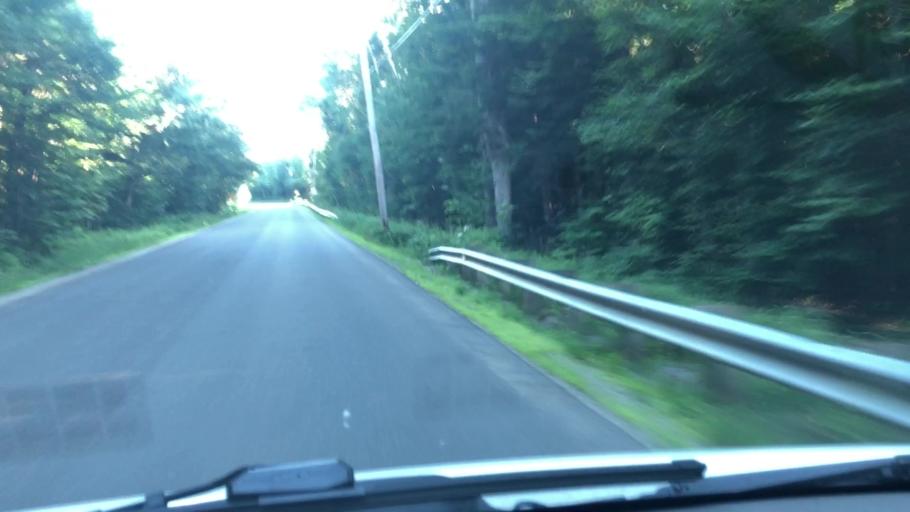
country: US
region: Massachusetts
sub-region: Berkshire County
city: Hinsdale
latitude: 42.4480
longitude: -72.9775
